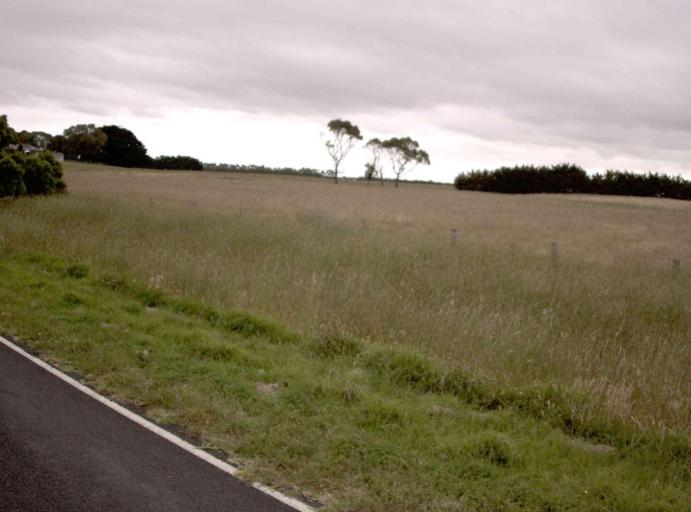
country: AU
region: Victoria
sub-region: Wellington
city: Sale
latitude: -38.5384
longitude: 146.8884
